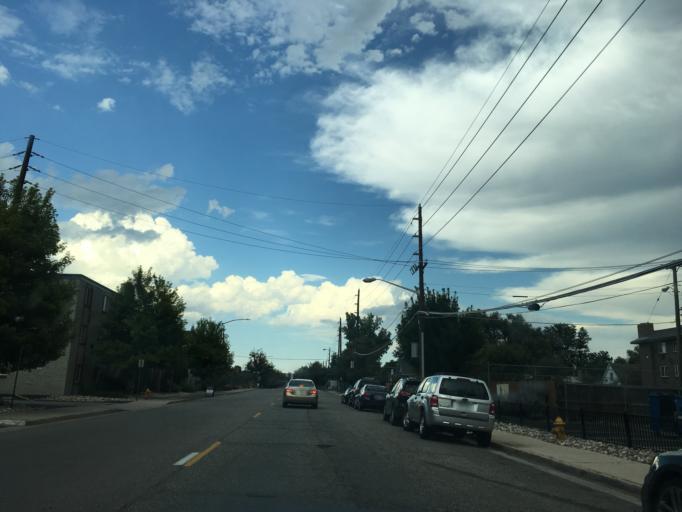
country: US
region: Colorado
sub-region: Arapahoe County
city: Glendale
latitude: 39.6966
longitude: -104.9333
